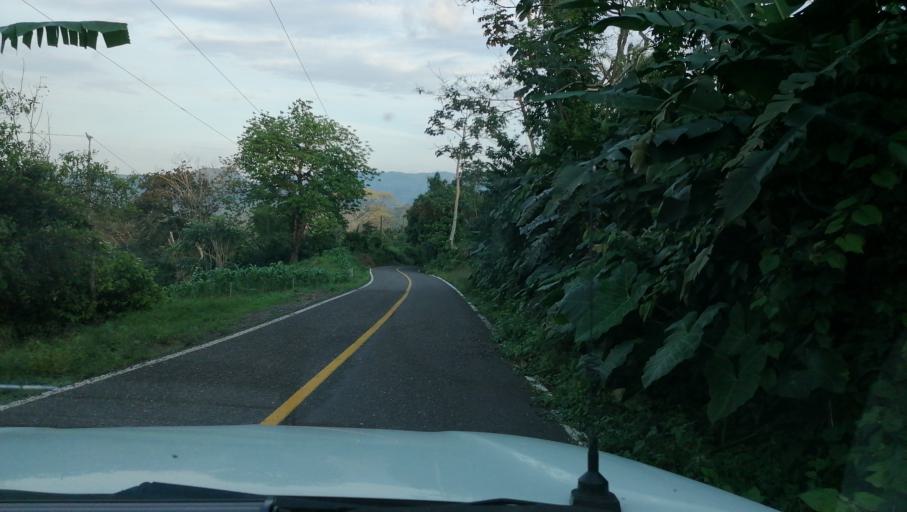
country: MX
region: Chiapas
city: Pichucalco
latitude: 17.5065
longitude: -93.2168
